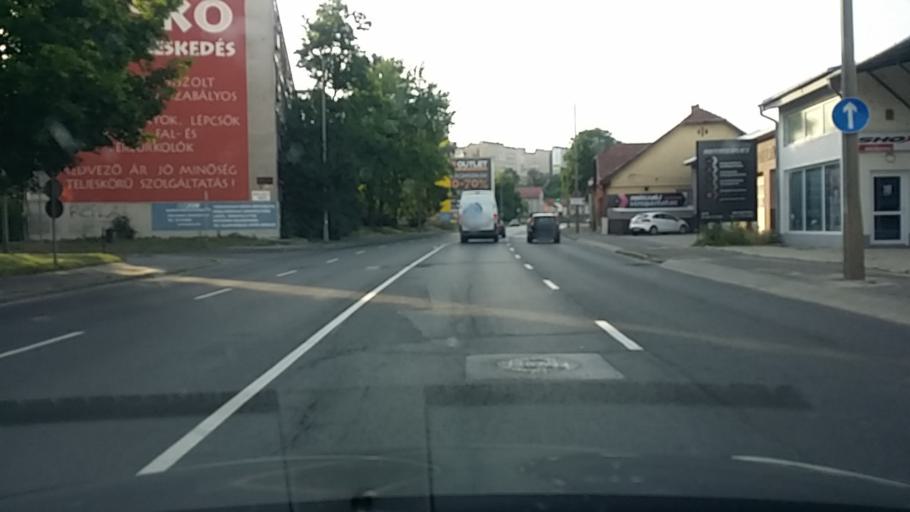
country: HU
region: Borsod-Abauj-Zemplen
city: Miskolc
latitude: 48.0746
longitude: 20.7867
